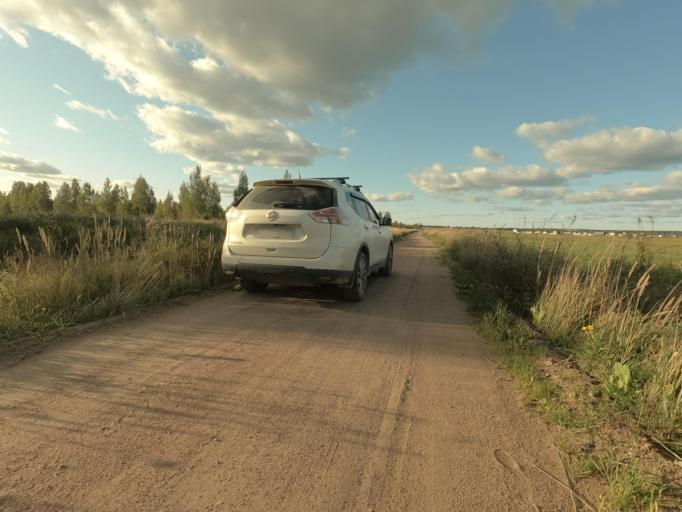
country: RU
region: Leningrad
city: Imeni Sverdlova
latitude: 59.8609
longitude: 30.7310
